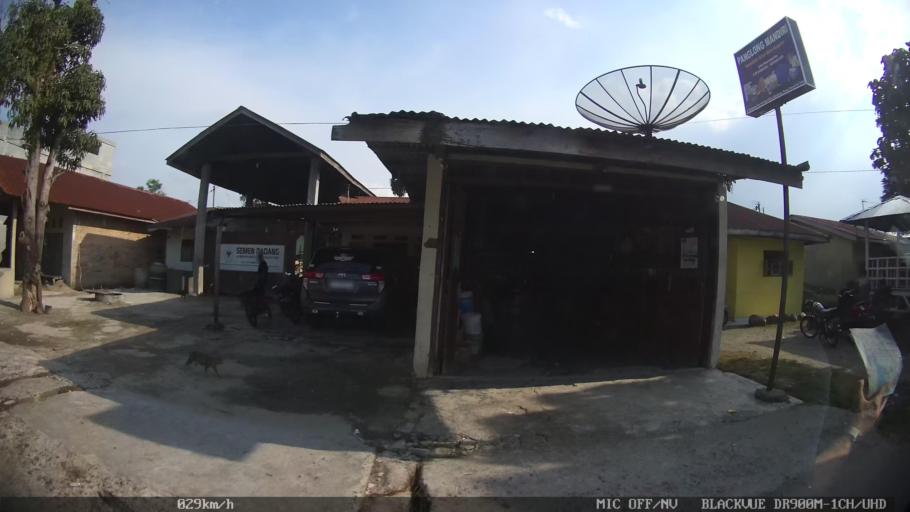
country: ID
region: North Sumatra
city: Medan
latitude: 3.5940
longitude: 98.7671
